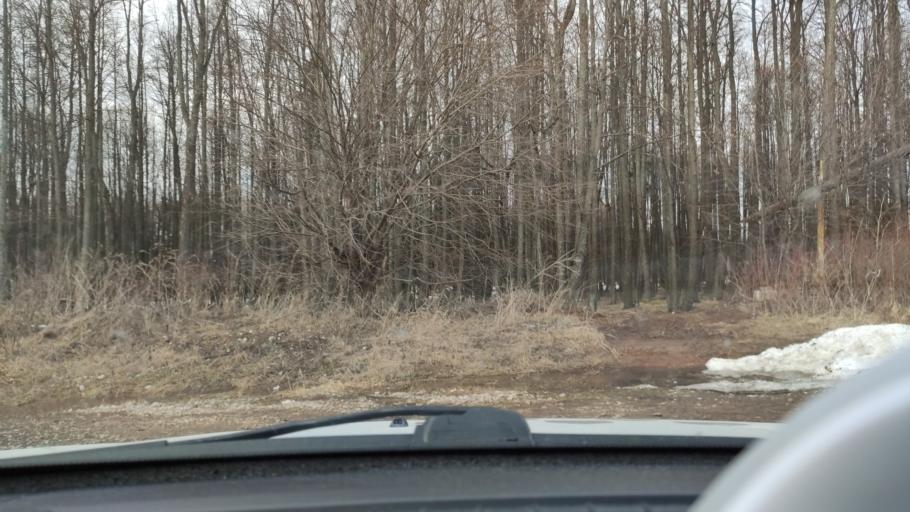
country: RU
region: Perm
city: Ferma
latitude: 57.8841
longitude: 56.3387
